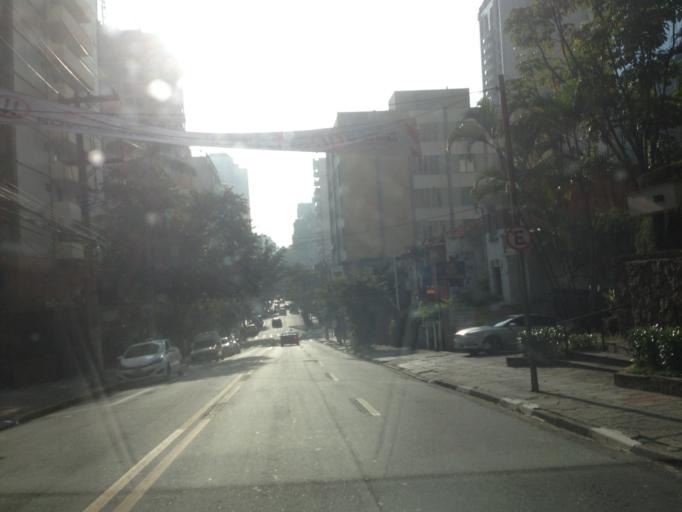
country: BR
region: Sao Paulo
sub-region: Sao Paulo
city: Sao Paulo
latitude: -23.5673
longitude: -46.6534
